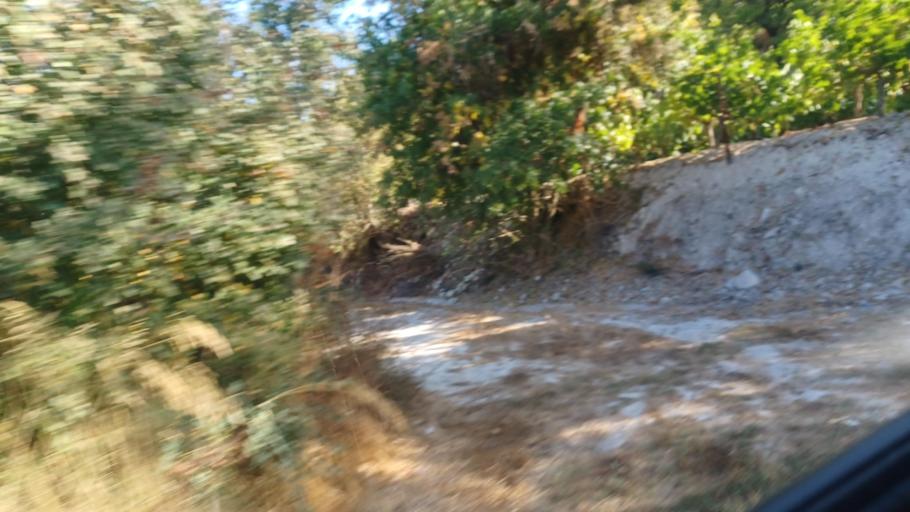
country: CY
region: Pafos
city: Mesogi
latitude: 34.8445
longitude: 32.4836
